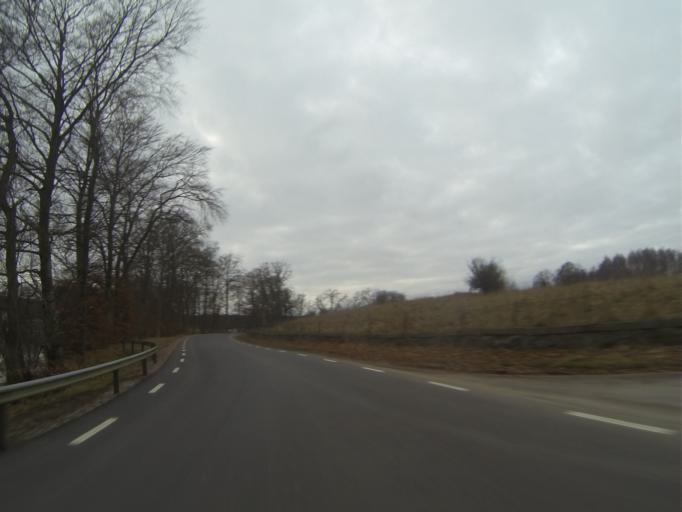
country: SE
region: Skane
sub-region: Lunds Kommun
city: Genarp
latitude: 55.5799
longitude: 13.4325
